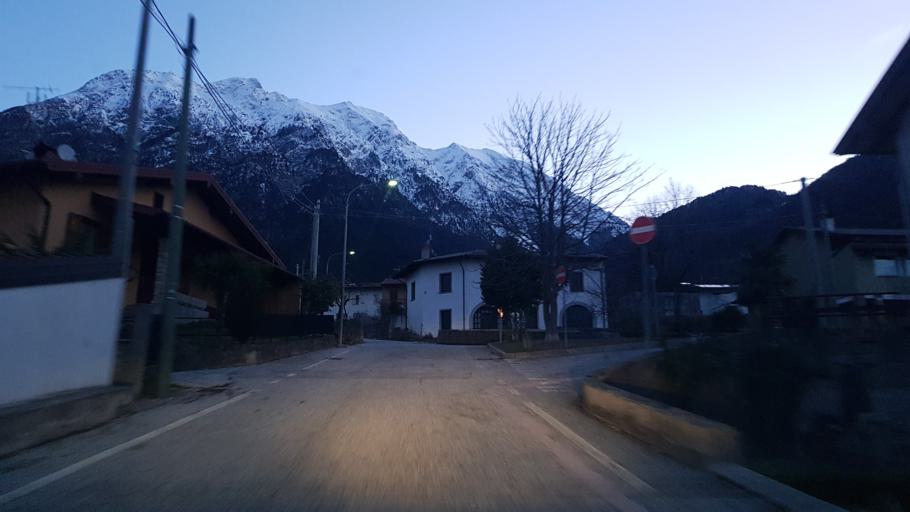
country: IT
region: Friuli Venezia Giulia
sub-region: Provincia di Udine
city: Gemona
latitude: 46.2825
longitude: 13.1426
